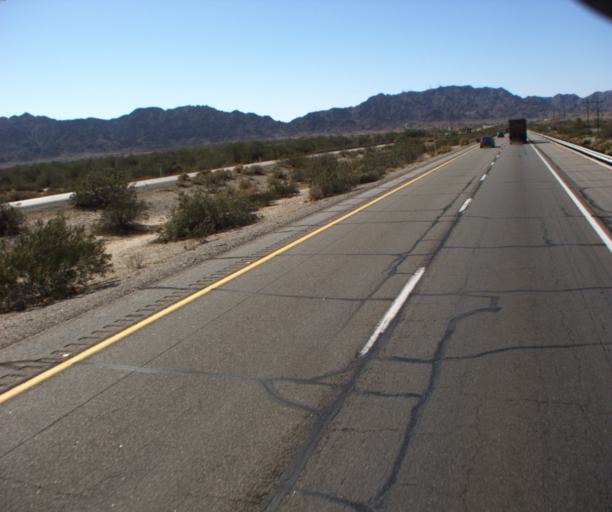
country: US
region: Arizona
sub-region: Yuma County
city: Wellton
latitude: 32.6639
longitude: -114.2702
